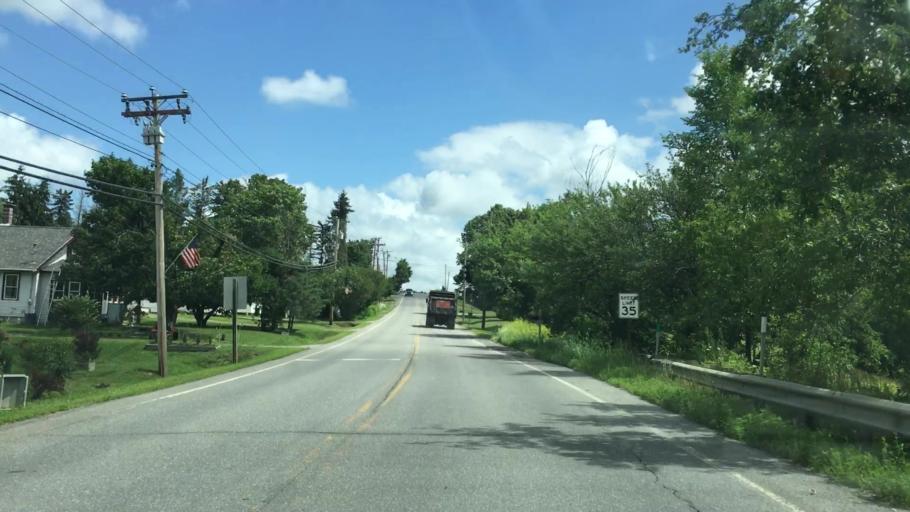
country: US
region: Maine
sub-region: Penobscot County
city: Carmel
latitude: 44.7977
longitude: -69.0466
